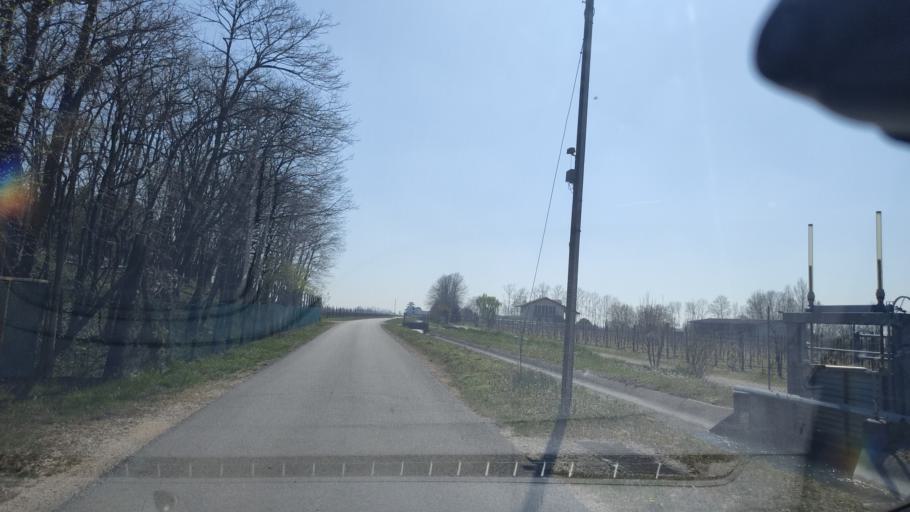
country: IT
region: Friuli Venezia Giulia
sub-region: Provincia di Pordenone
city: Vigonovo-Fontanafredda
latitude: 46.0180
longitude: 12.5496
